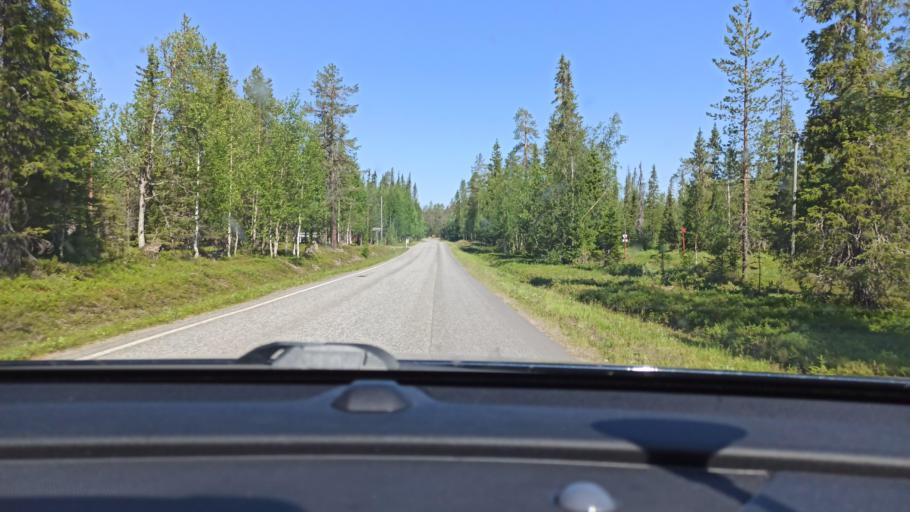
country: FI
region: Lapland
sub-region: Tunturi-Lappi
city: Kolari
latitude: 67.6657
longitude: 24.1611
